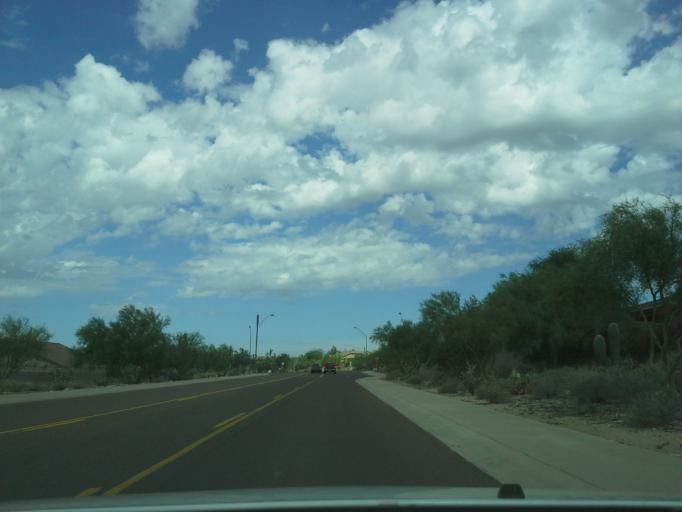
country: US
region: Arizona
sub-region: Maricopa County
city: Fountain Hills
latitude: 33.6318
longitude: -111.8461
